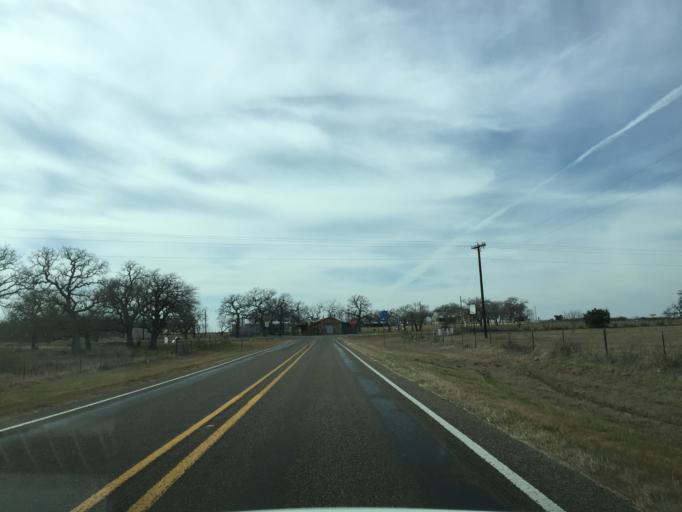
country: US
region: Texas
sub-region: Gillespie County
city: Fredericksburg
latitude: 30.4132
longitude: -98.7353
